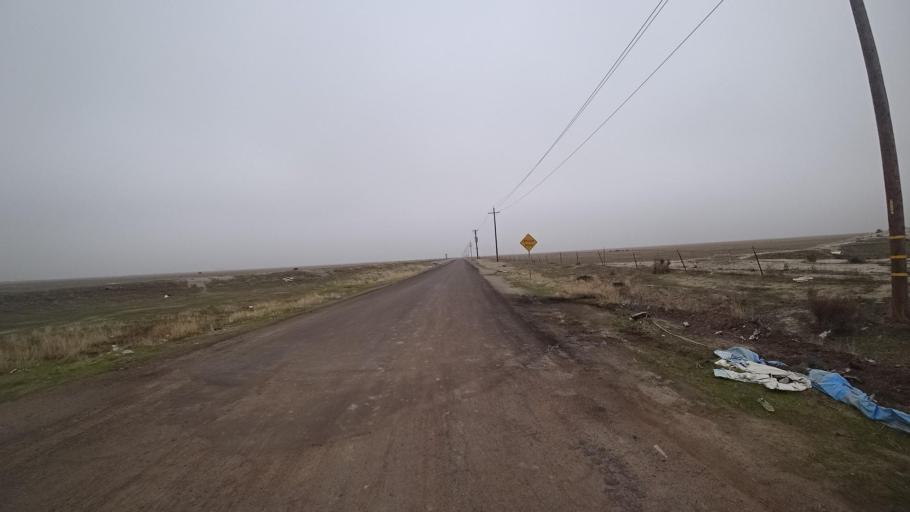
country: US
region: California
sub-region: Tulare County
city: Alpaugh
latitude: 35.7899
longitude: -119.4723
